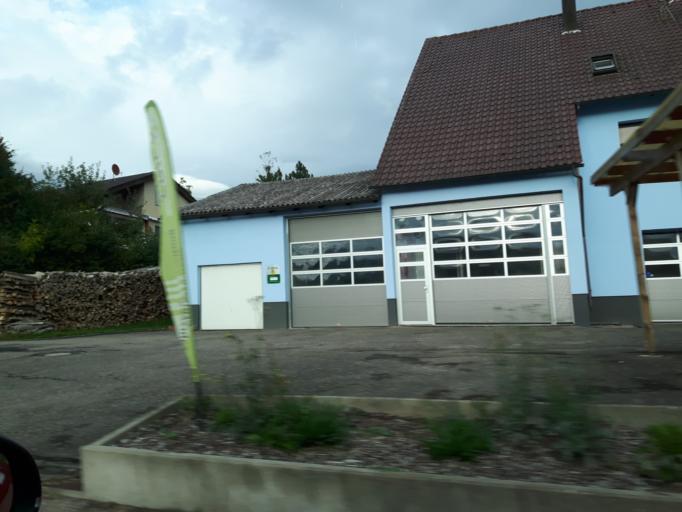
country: DE
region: Baden-Wuerttemberg
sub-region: Karlsruhe Region
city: Sternenfels
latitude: 49.0055
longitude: 8.8597
